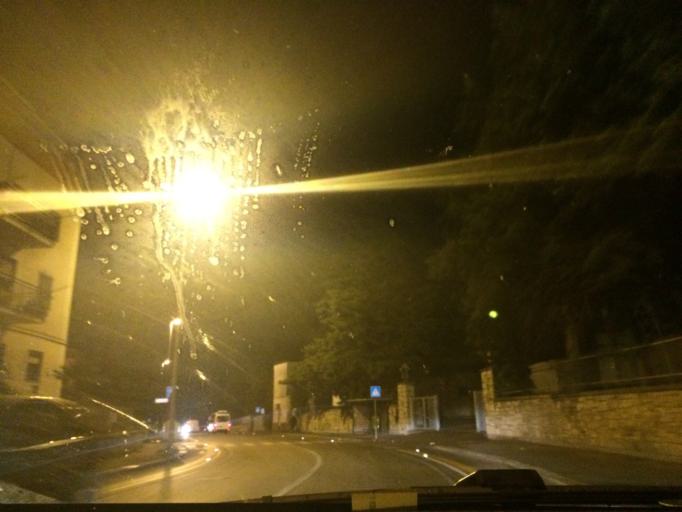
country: IT
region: Basilicate
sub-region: Provincia di Matera
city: Matera
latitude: 40.6601
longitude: 16.6009
